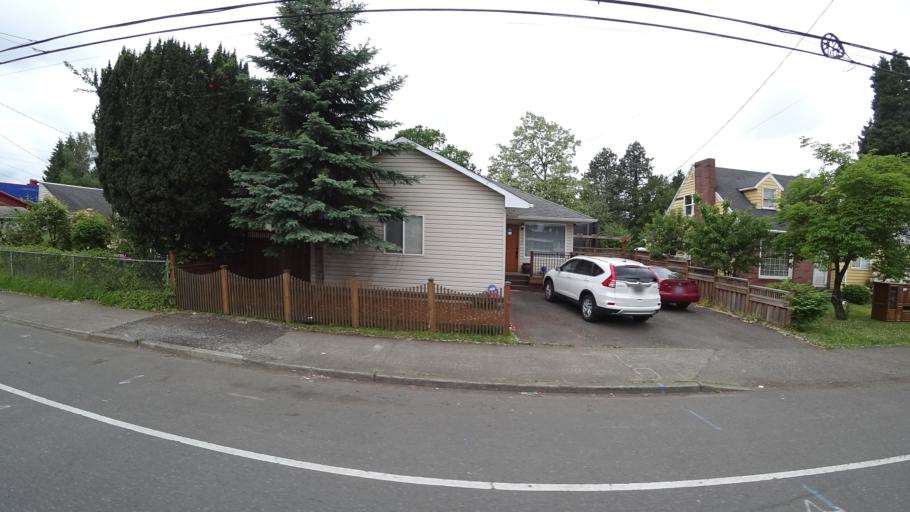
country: US
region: Oregon
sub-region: Multnomah County
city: Lents
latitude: 45.5058
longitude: -122.5690
